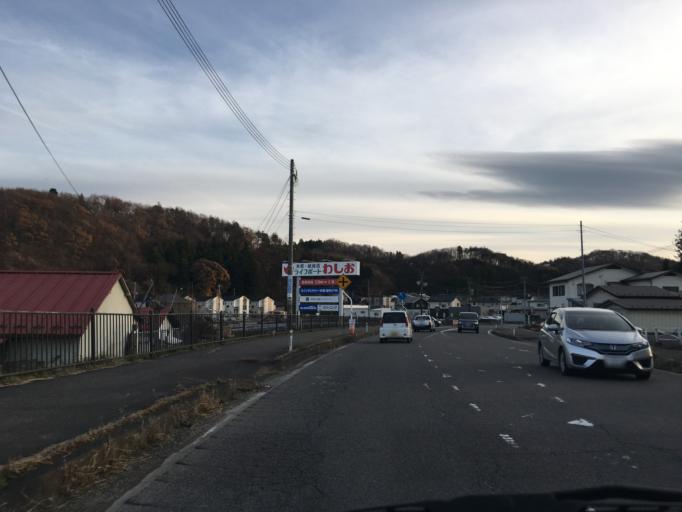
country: JP
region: Fukushima
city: Ishikawa
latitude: 37.1185
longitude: 140.2283
